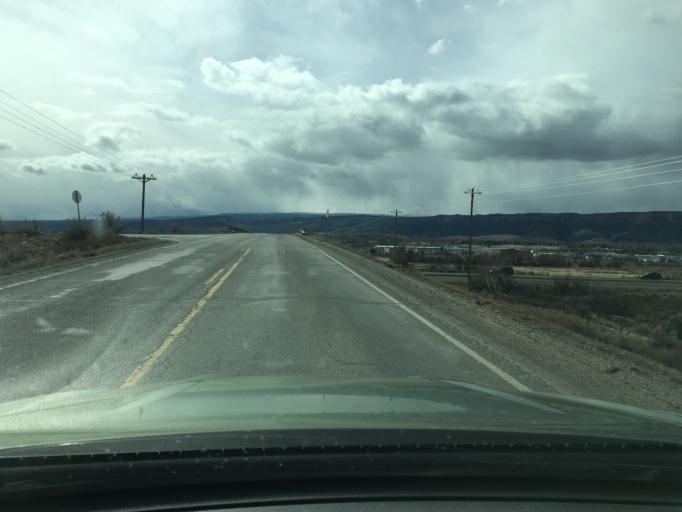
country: US
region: Colorado
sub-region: Mesa County
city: Redlands
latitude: 39.1150
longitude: -108.6267
